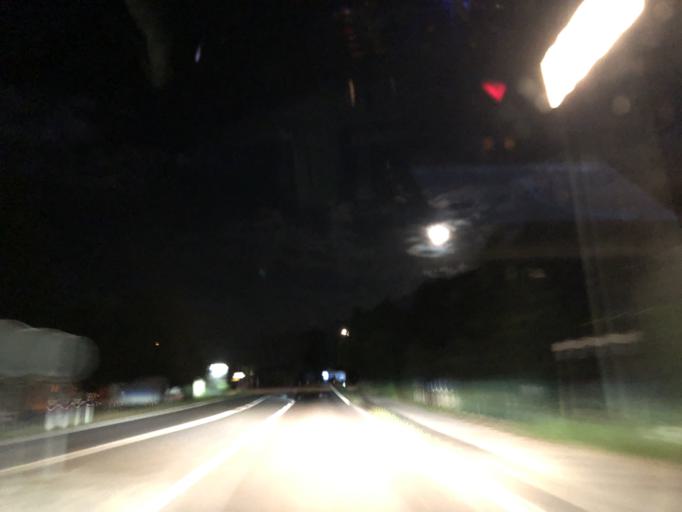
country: DE
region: Bavaria
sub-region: Upper Bavaria
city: Finsing
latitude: 48.2303
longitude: 11.8143
